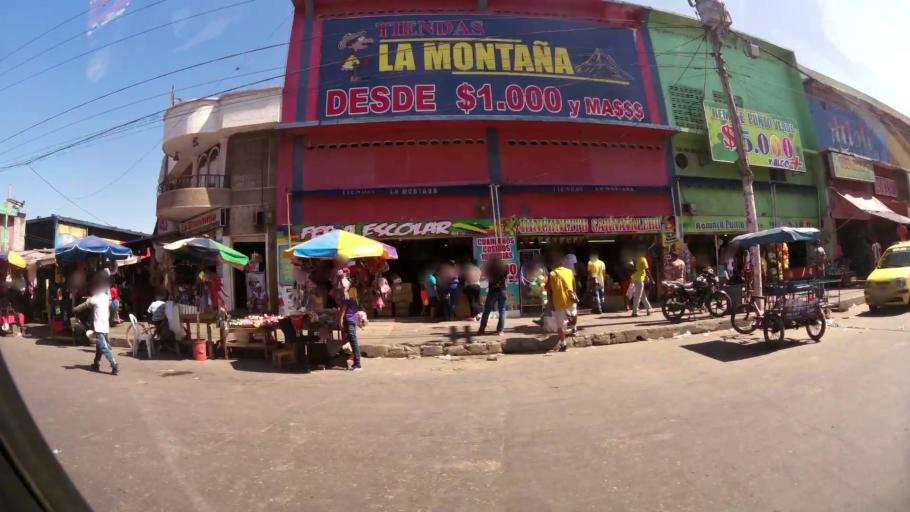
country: CO
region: Atlantico
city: Barranquilla
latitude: 10.9782
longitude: -74.7760
